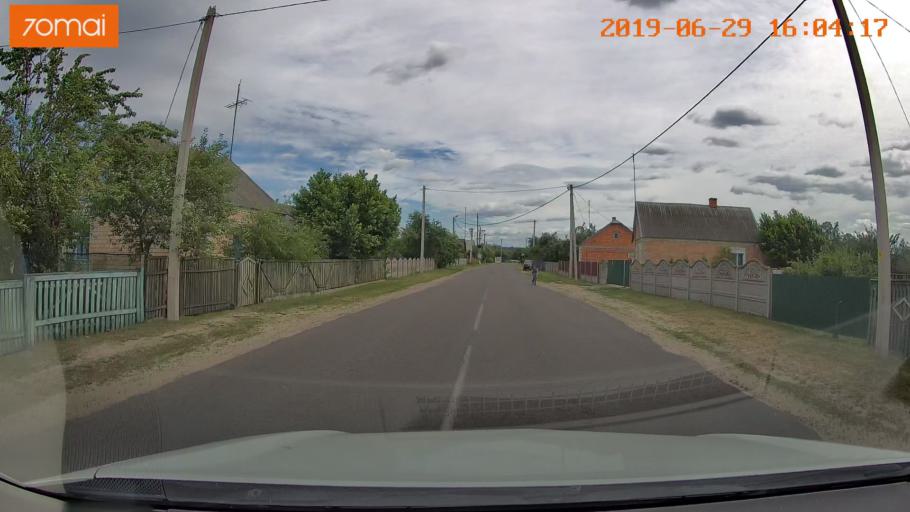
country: BY
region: Brest
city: Luninyets
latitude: 52.2239
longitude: 27.0241
